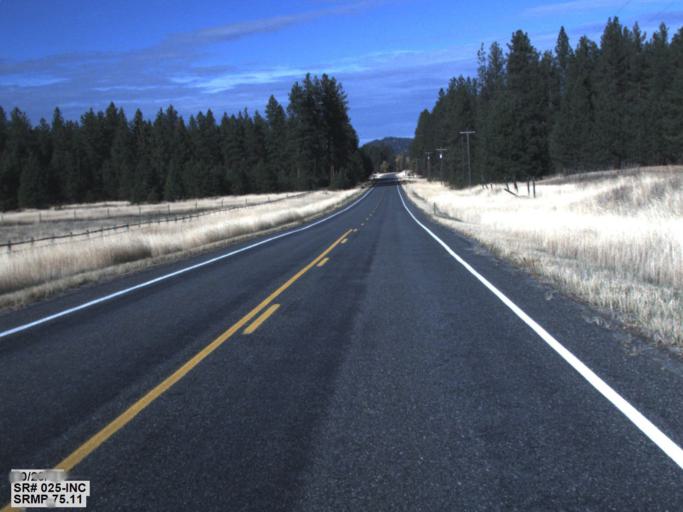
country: US
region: Washington
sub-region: Stevens County
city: Kettle Falls
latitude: 48.5422
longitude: -118.1305
